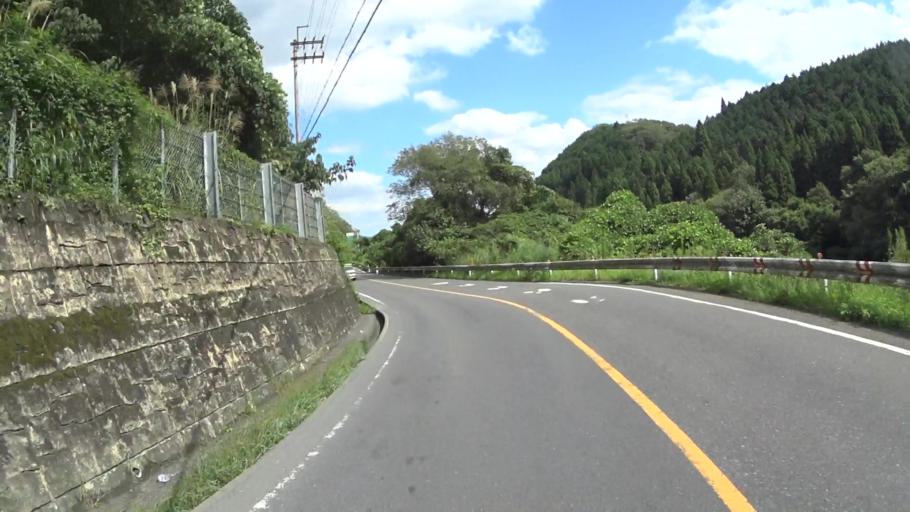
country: JP
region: Kyoto
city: Uji
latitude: 34.9165
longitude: 135.8747
